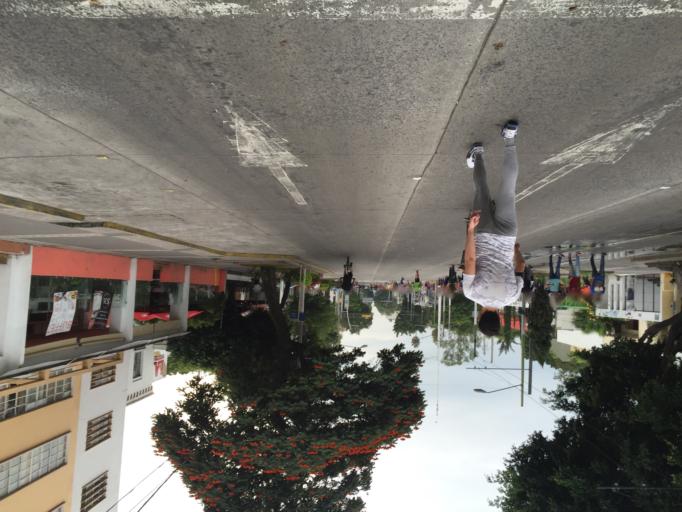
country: MX
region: Jalisco
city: Guadalajara
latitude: 20.6748
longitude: -103.3575
